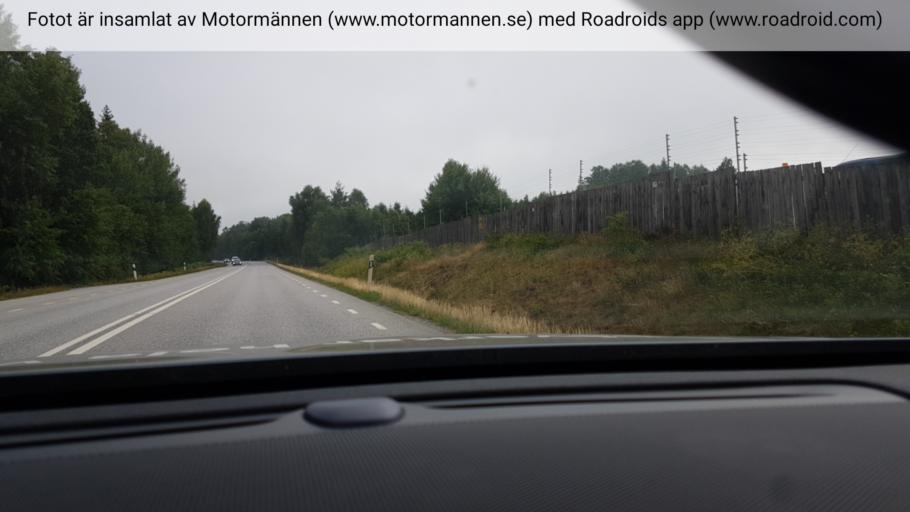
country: SE
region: Skane
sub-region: Hassleholms Kommun
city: Bjarnum
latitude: 56.2514
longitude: 13.7169
